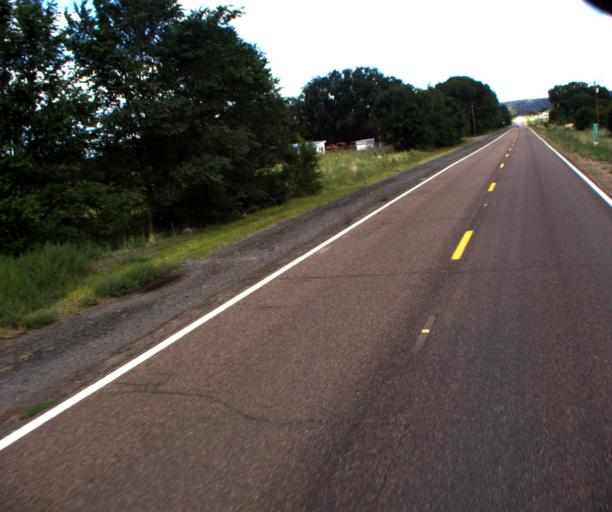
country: US
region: Arizona
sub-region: Apache County
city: Eagar
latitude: 34.1109
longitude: -109.2780
